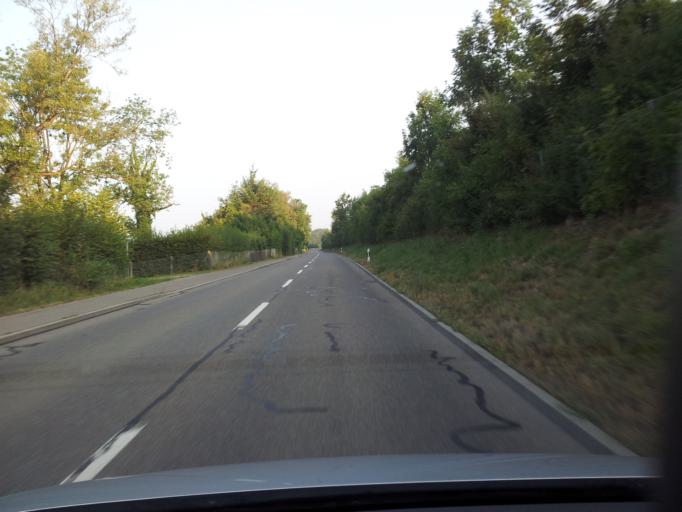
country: CH
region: Lucerne
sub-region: Sursee District
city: Schenkon
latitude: 47.1589
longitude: 8.1527
